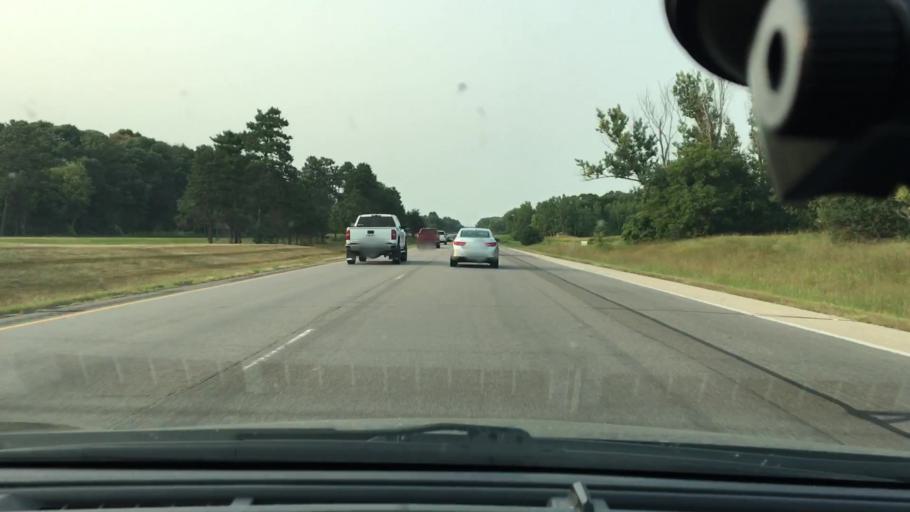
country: US
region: Minnesota
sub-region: Sherburne County
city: Zimmerman
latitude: 45.5059
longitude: -93.5823
